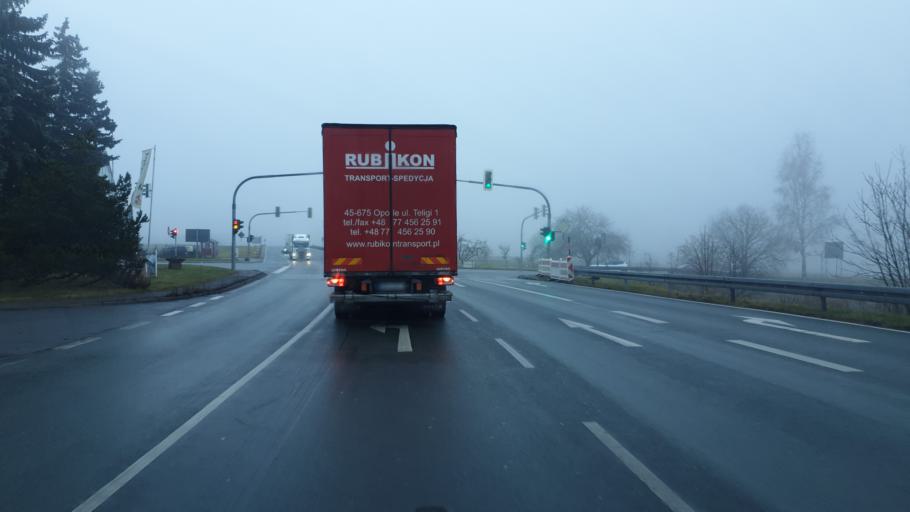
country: DE
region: Saxony
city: Grossolbersdorf
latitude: 50.6807
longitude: 13.1192
